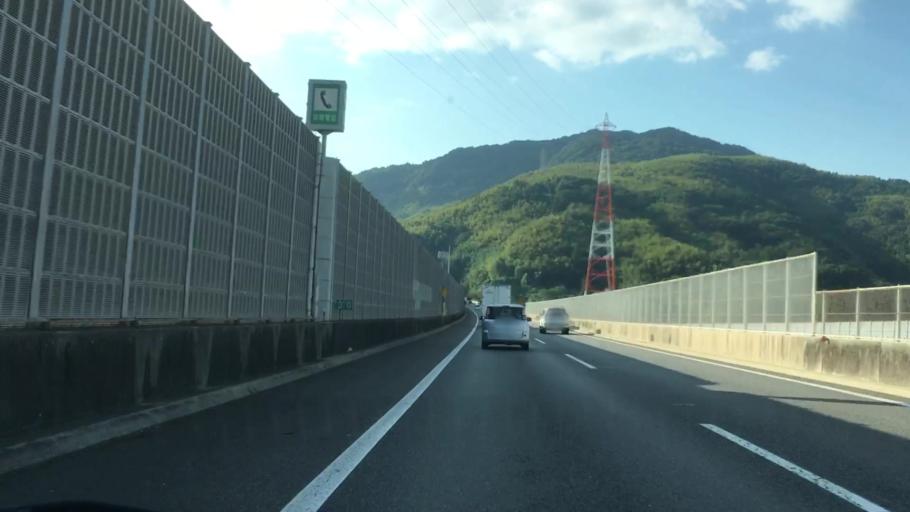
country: JP
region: Yamaguchi
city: Tokuyama
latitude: 34.0861
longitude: 131.7817
